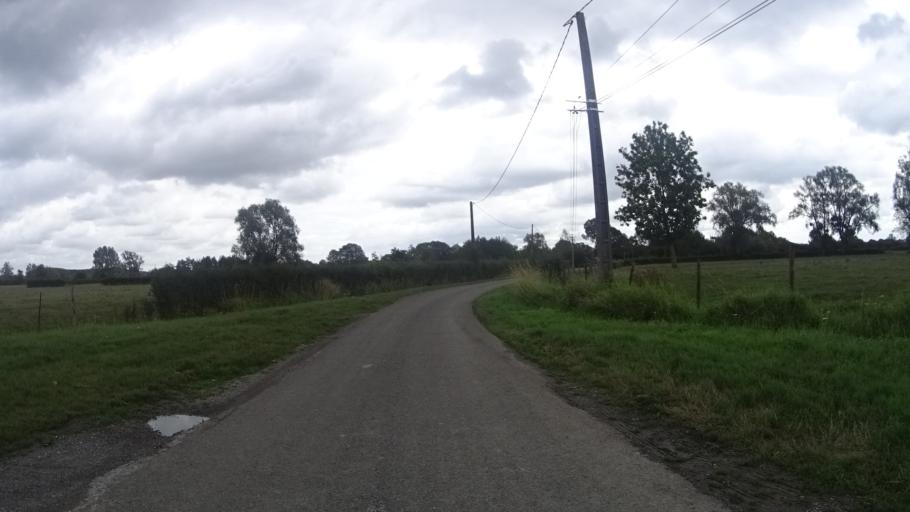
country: FR
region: Nord-Pas-de-Calais
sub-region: Departement du Nord
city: Maroilles
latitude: 50.1428
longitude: 3.7385
